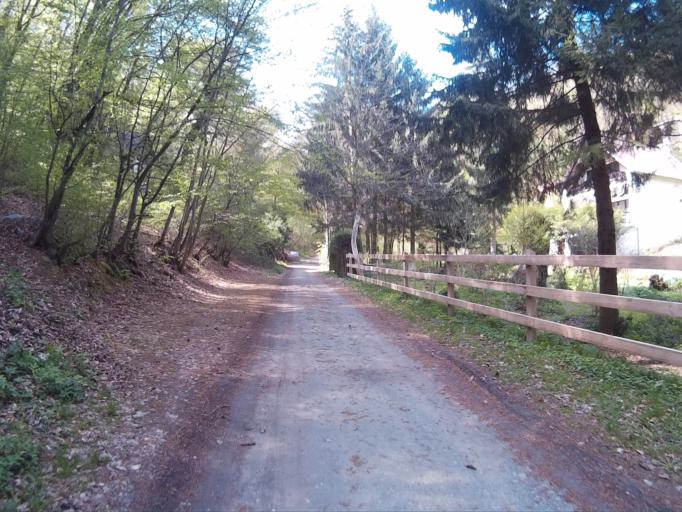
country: AT
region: Burgenland
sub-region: Politischer Bezirk Oberwart
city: Rechnitz
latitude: 47.3468
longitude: 16.4828
